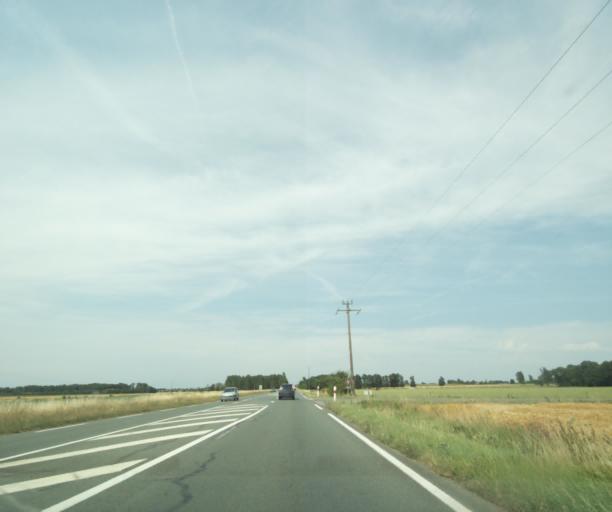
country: FR
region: Centre
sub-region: Departement d'Indre-et-Loire
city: Sorigny
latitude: 47.2111
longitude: 0.6768
